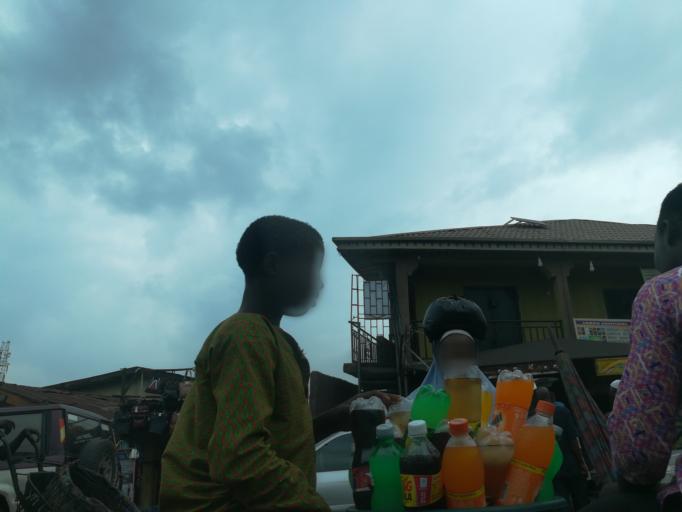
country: NG
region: Lagos
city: Ojota
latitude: 6.6096
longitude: 3.3960
